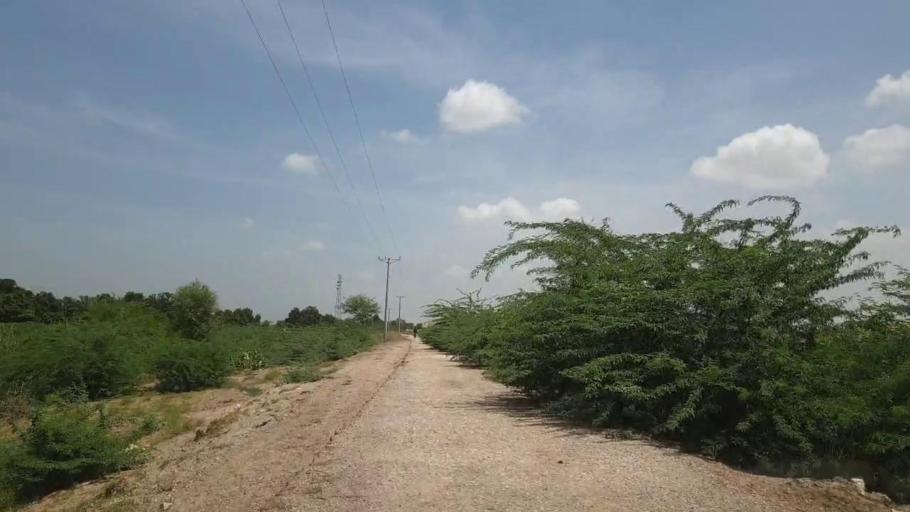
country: PK
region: Sindh
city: Kot Diji
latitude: 27.1429
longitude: 69.0137
